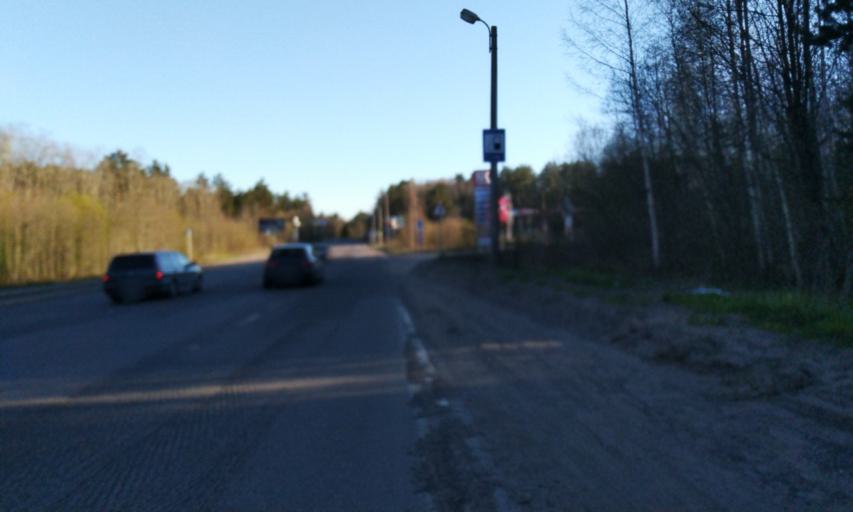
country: RU
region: Leningrad
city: Toksovo
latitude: 60.1371
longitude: 30.5284
